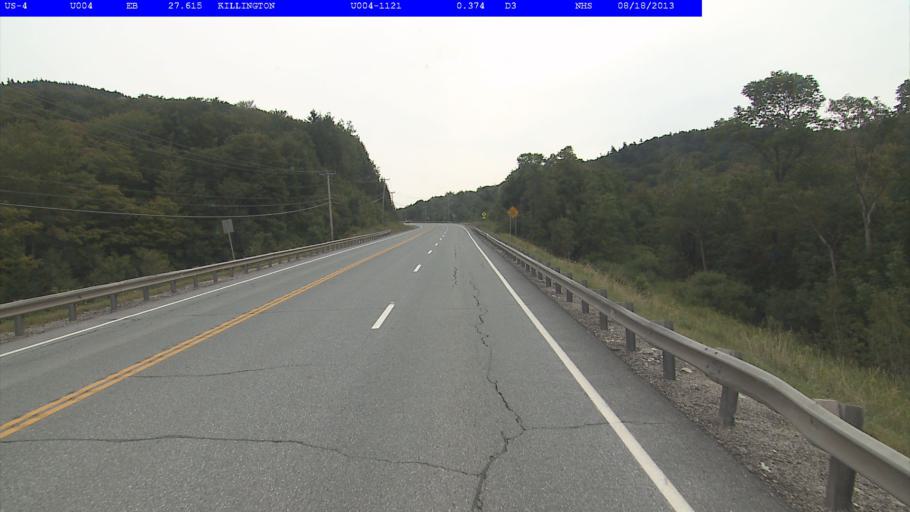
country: US
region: Vermont
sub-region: Rutland County
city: Rutland
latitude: 43.6639
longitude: -72.8392
